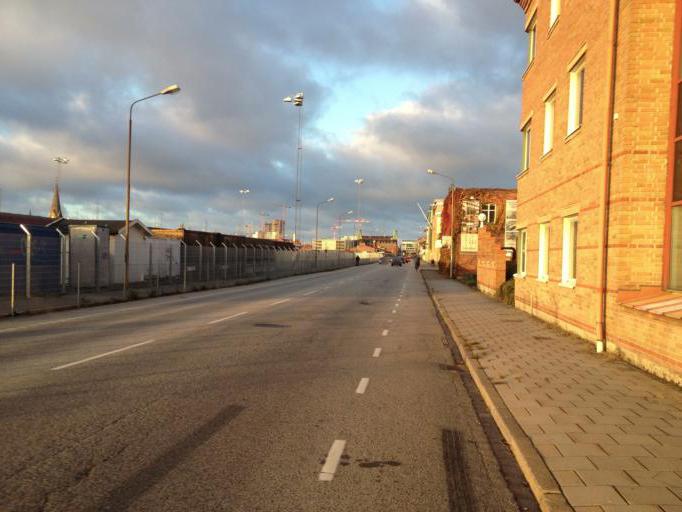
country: SE
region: Skane
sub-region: Malmo
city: Malmoe
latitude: 55.6117
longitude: 13.0134
